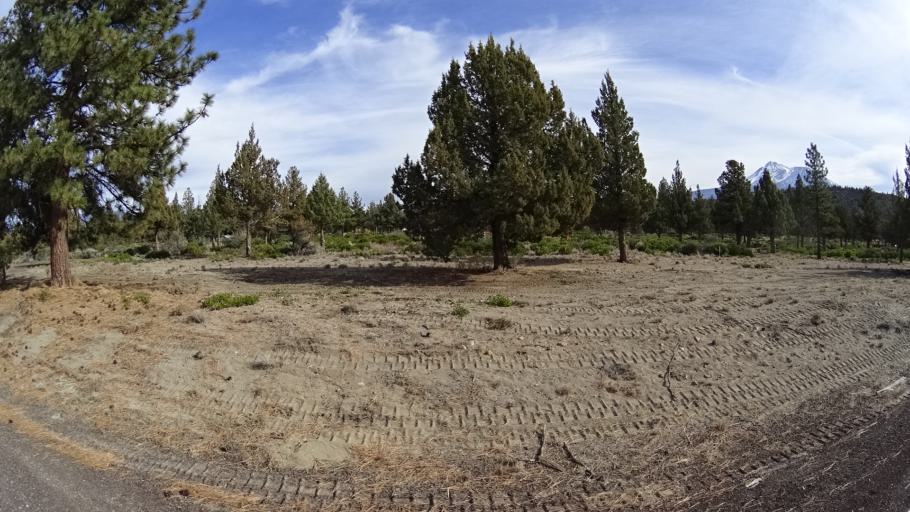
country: US
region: California
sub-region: Siskiyou County
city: Weed
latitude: 41.5299
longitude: -122.3647
